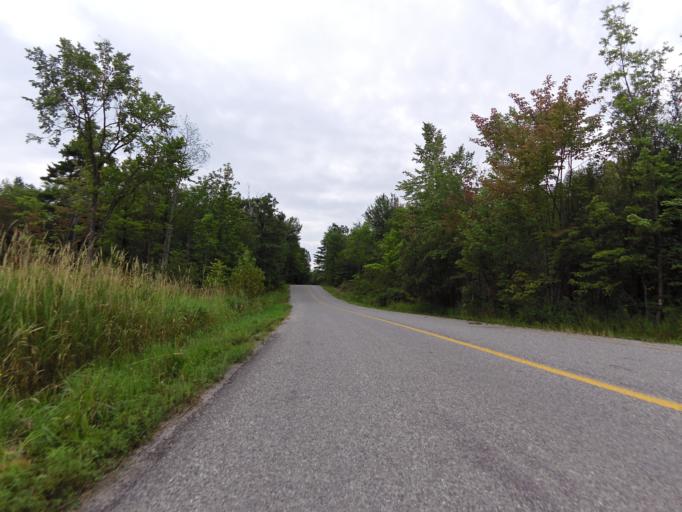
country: CA
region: Ontario
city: Kingston
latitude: 44.5938
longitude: -76.6386
